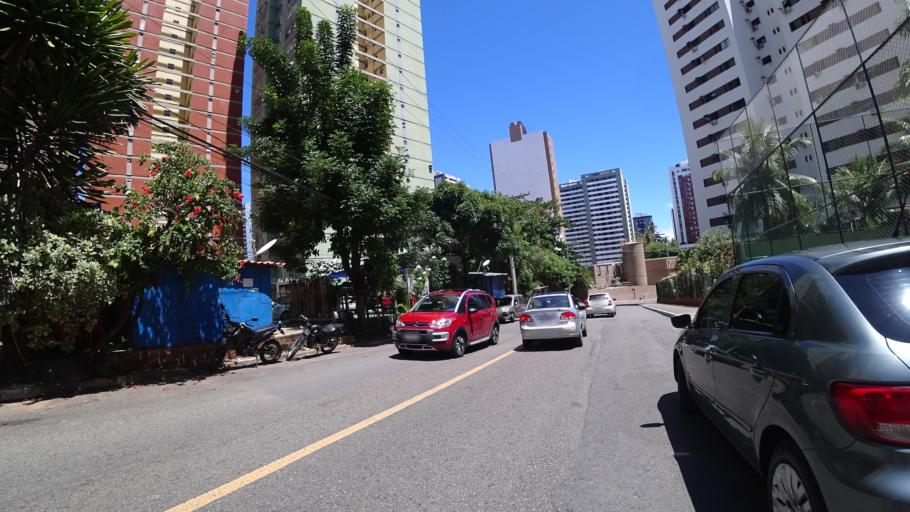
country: BR
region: Bahia
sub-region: Salvador
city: Salvador
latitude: -13.0019
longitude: -38.4636
